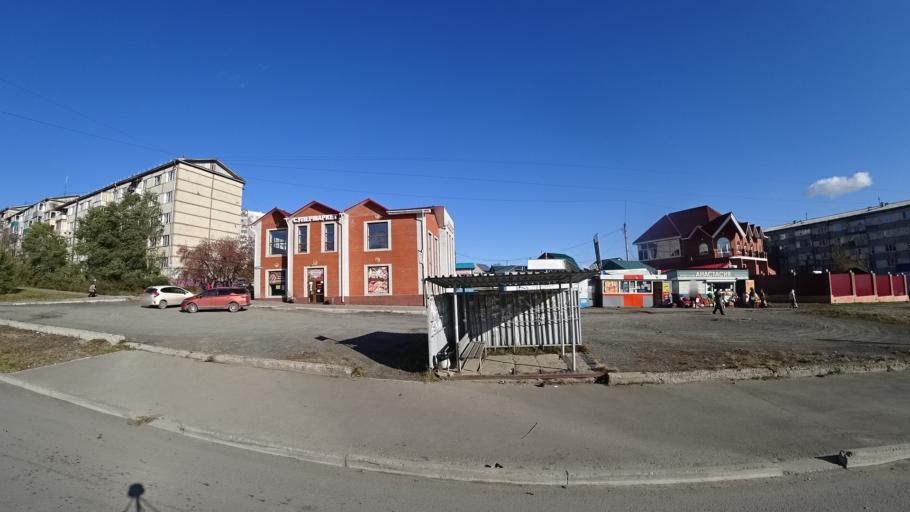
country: RU
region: Khabarovsk Krai
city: Amursk
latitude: 50.2376
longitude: 136.9111
